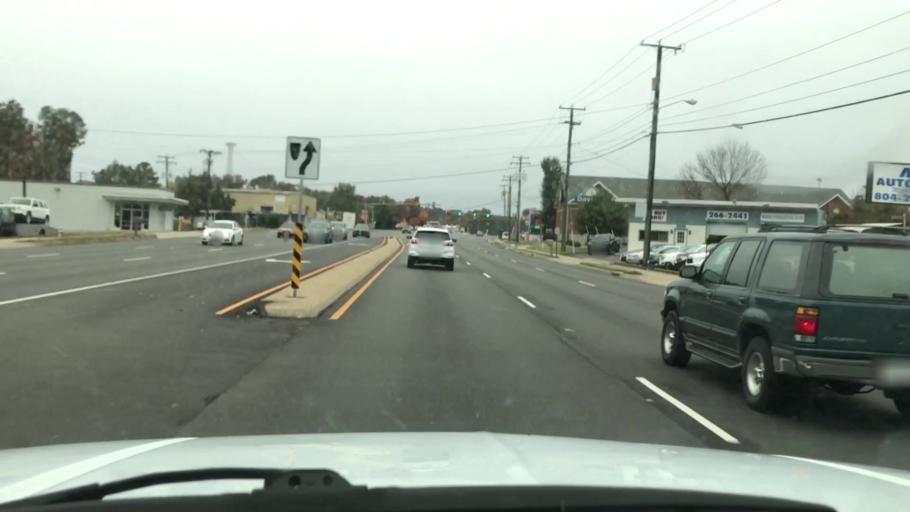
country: US
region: Virginia
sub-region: Henrico County
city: Chamberlayne
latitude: 37.6401
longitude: -77.4598
